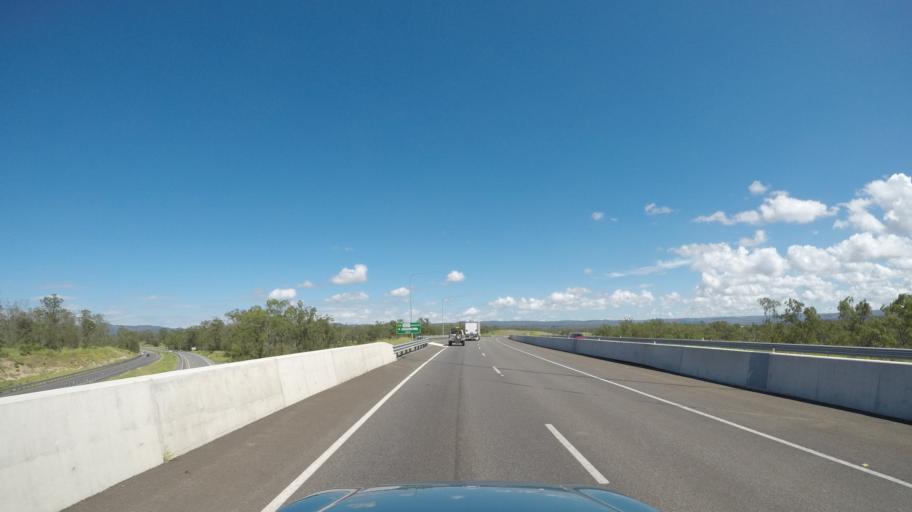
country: AU
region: Queensland
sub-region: Toowoomba
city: Rangeville
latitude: -27.5436
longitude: 152.0803
